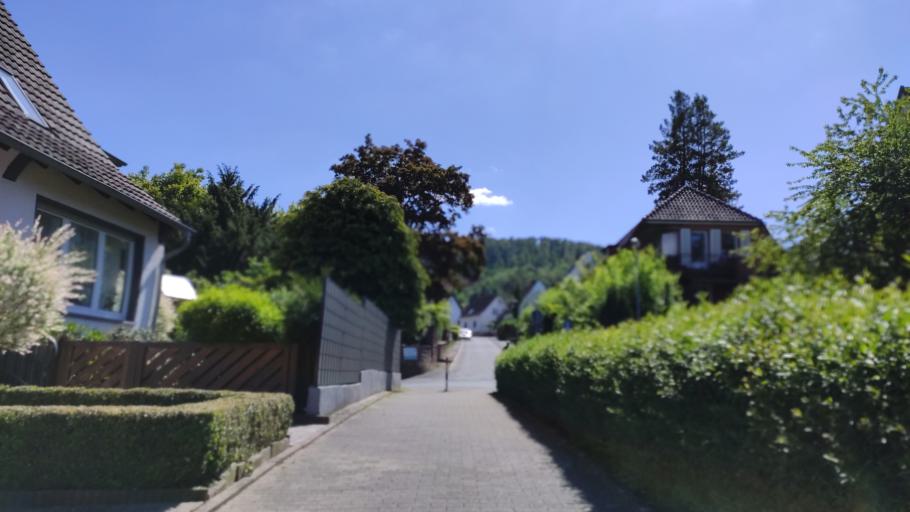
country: DE
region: North Rhine-Westphalia
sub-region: Regierungsbezirk Detmold
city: Hoexter
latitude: 51.7688
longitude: 9.3761
